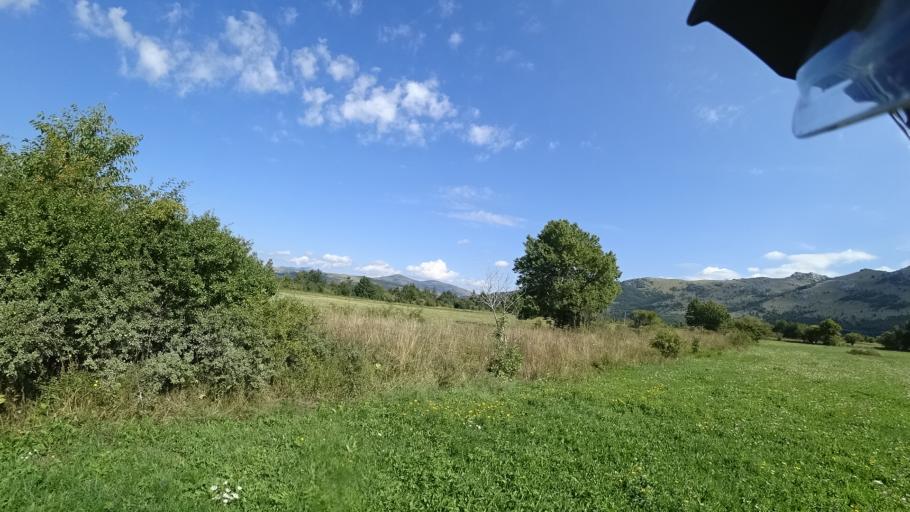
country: HR
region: Zadarska
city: Gracac
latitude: 44.3390
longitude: 15.9557
